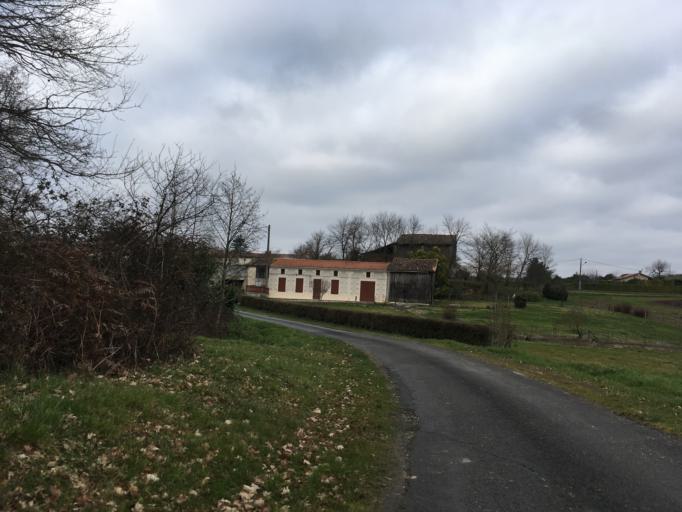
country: FR
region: Aquitaine
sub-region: Departement de la Gironde
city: Saint-Ciers-sur-Gironde
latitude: 45.3114
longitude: -0.5854
